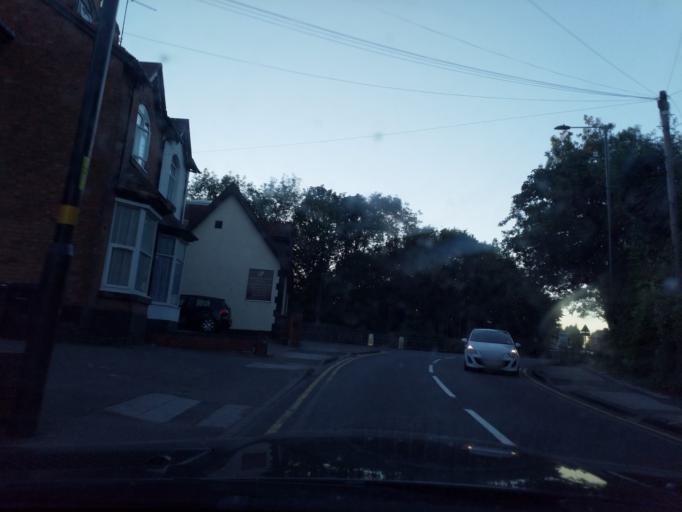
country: GB
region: England
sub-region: City and Borough of Birmingham
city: Acocks Green
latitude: 52.4555
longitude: -1.8188
